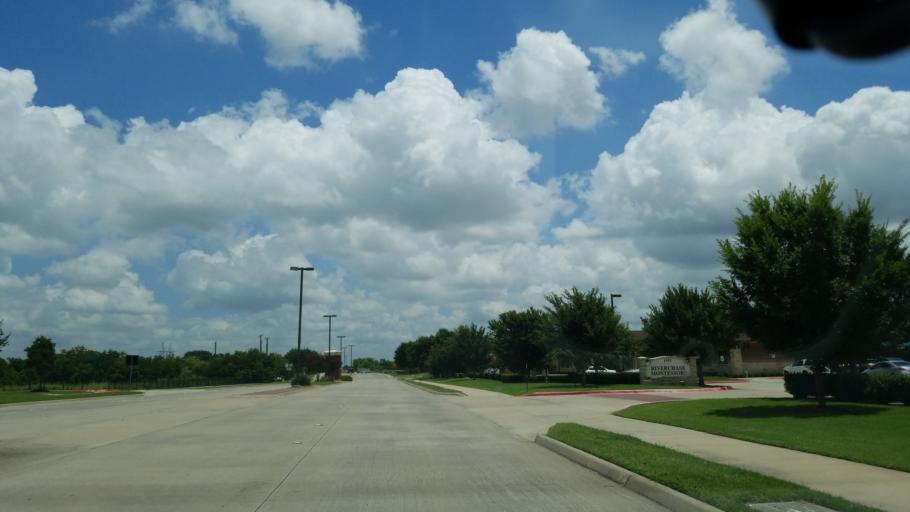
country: US
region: Texas
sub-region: Dallas County
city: Carrollton
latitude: 32.9659
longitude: -96.9481
